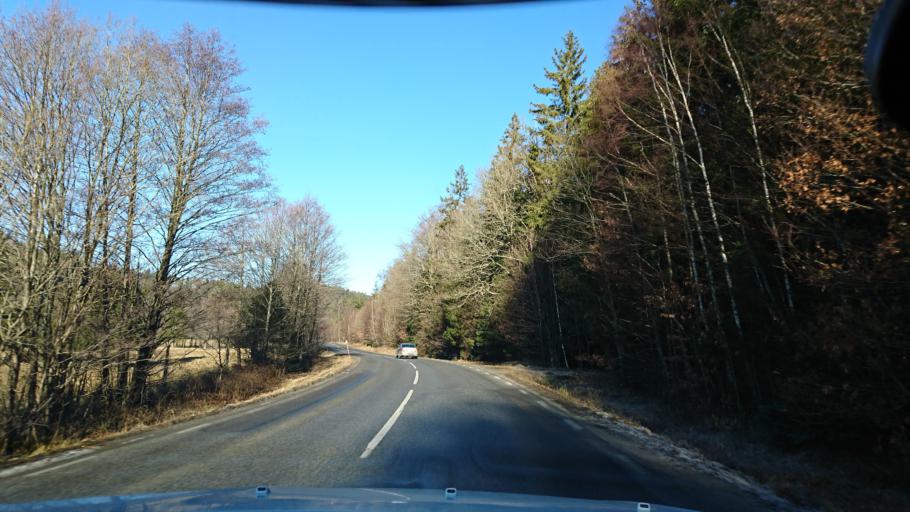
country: SE
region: Vaestra Goetaland
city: Svanesund
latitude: 58.1393
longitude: 11.8659
